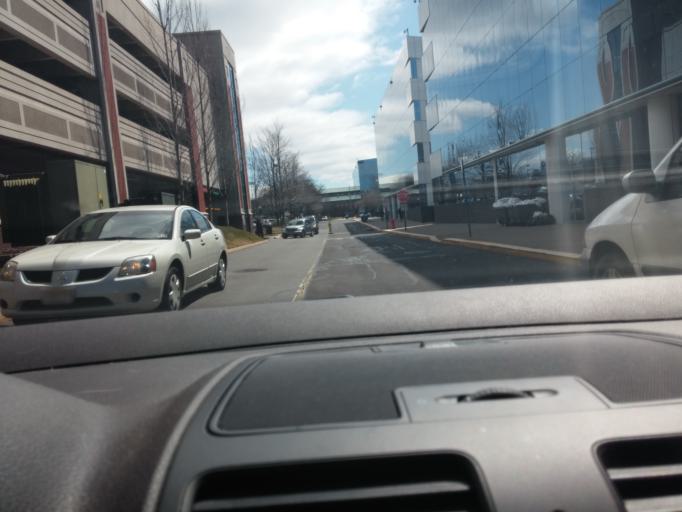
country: US
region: New Jersey
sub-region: Mercer County
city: Trenton
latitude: 40.2062
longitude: -74.7634
